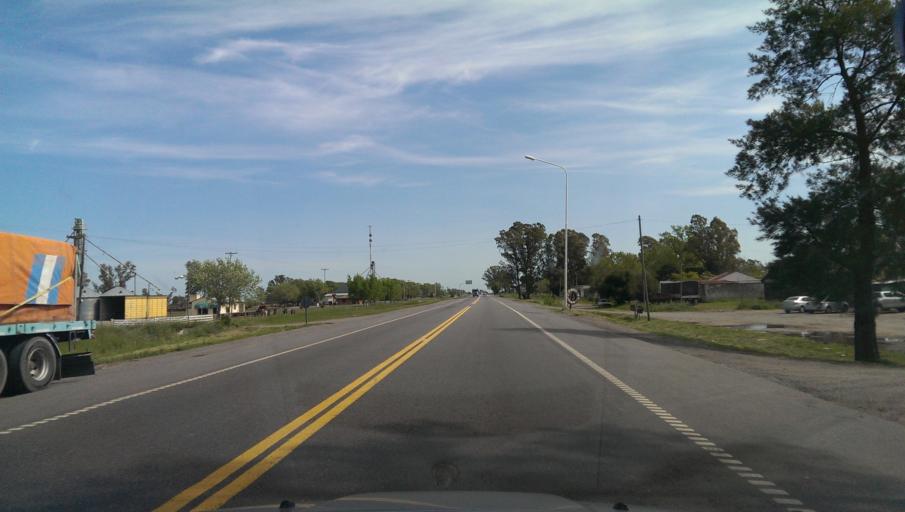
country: AR
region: Buenos Aires
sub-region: Partido de Azul
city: Azul
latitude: -36.3889
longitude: -59.4941
